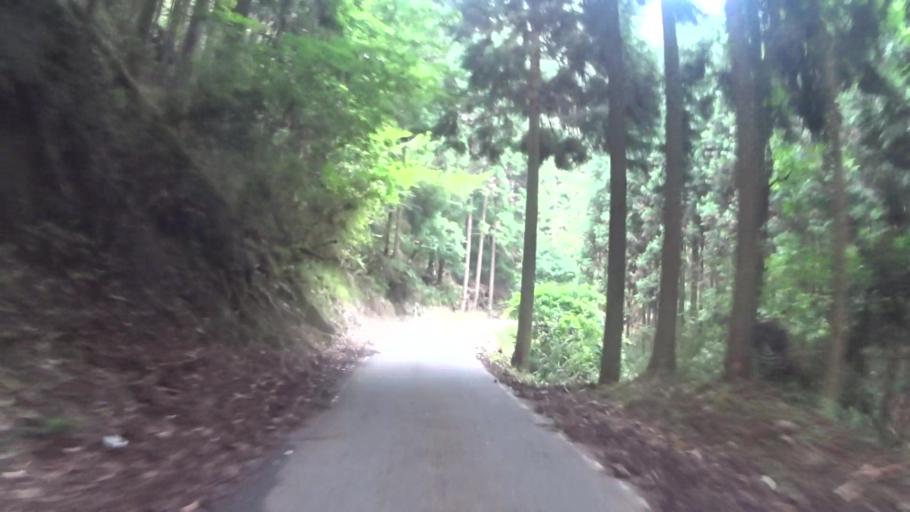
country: JP
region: Kyoto
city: Kameoka
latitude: 35.1509
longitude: 135.5726
